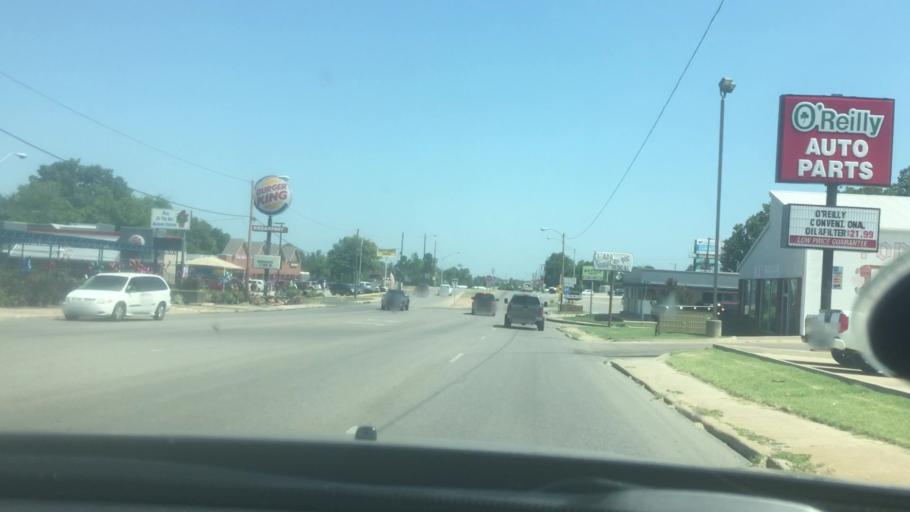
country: US
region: Oklahoma
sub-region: Pontotoc County
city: Ada
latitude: 34.7797
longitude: -96.6699
